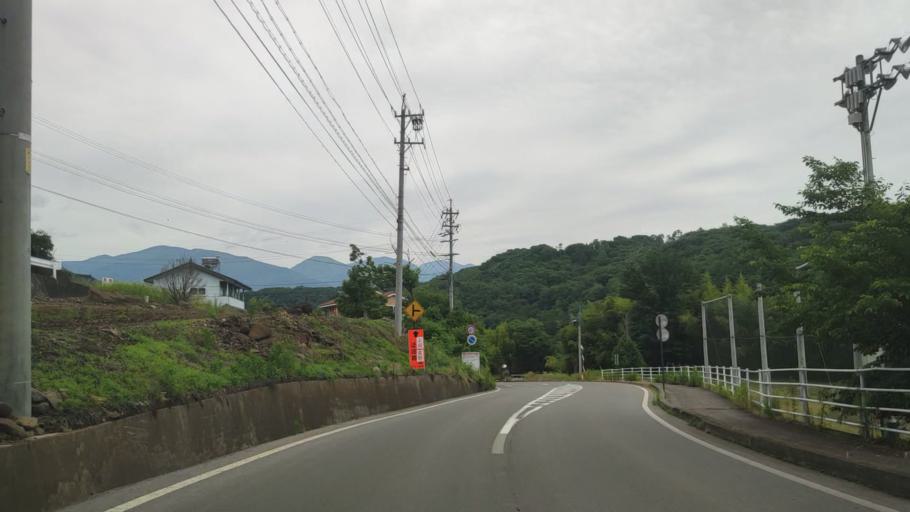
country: JP
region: Nagano
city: Kamimaruko
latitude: 36.3262
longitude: 138.3421
